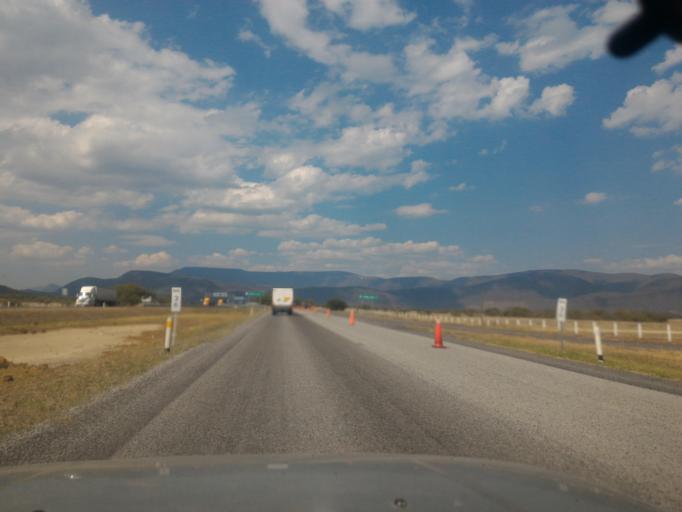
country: MX
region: Jalisco
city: Zacoalco de Torres
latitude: 20.1307
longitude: -103.5072
